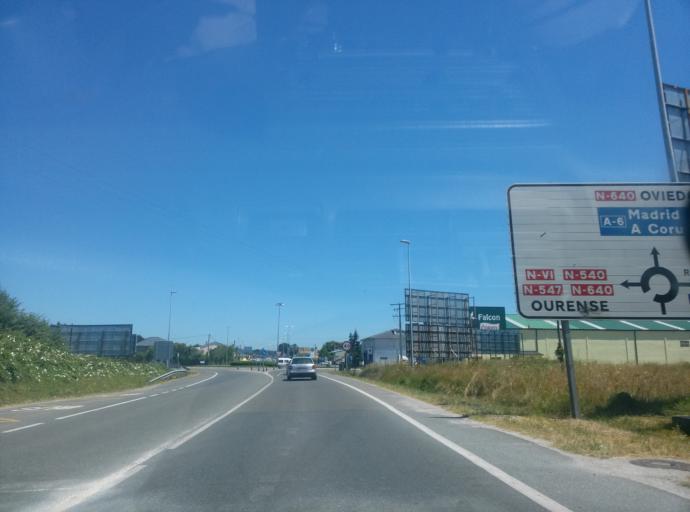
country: ES
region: Galicia
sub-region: Provincia de Lugo
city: Lugo
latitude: 43.0307
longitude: -7.5369
